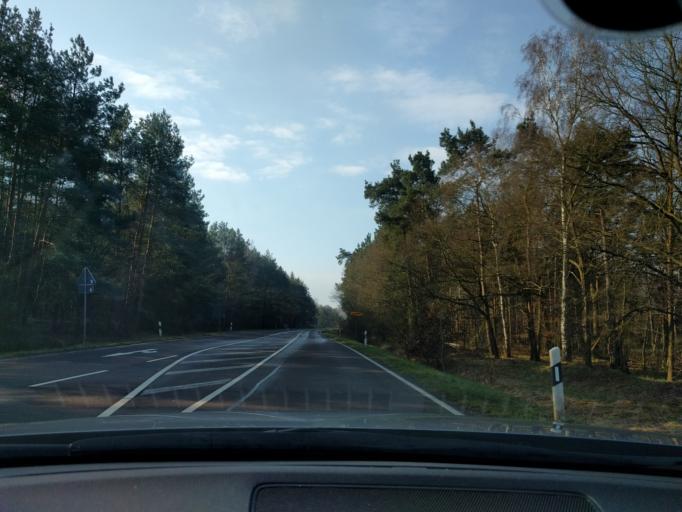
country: DE
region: Saxony-Anhalt
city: Arneburg
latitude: 52.6976
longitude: 11.9785
